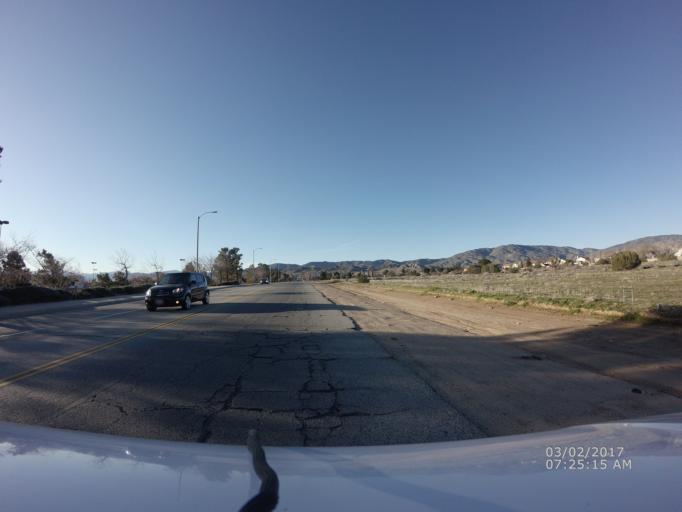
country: US
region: California
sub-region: Los Angeles County
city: Desert View Highlands
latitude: 34.6053
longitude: -118.1566
